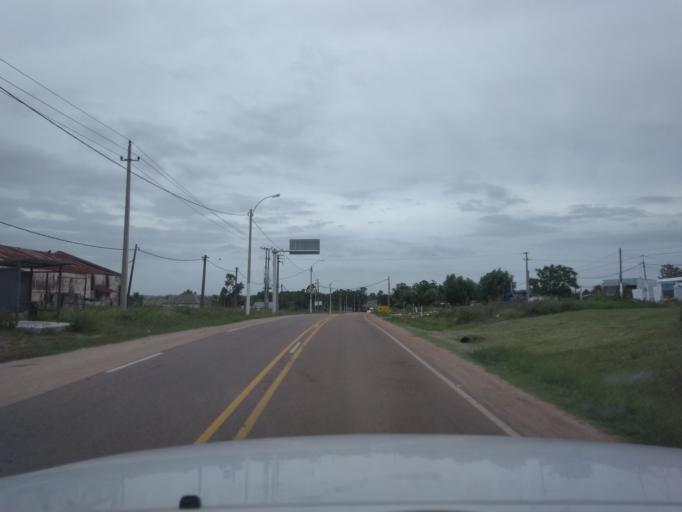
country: UY
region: Canelones
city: Tala
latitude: -34.3504
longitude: -55.7677
